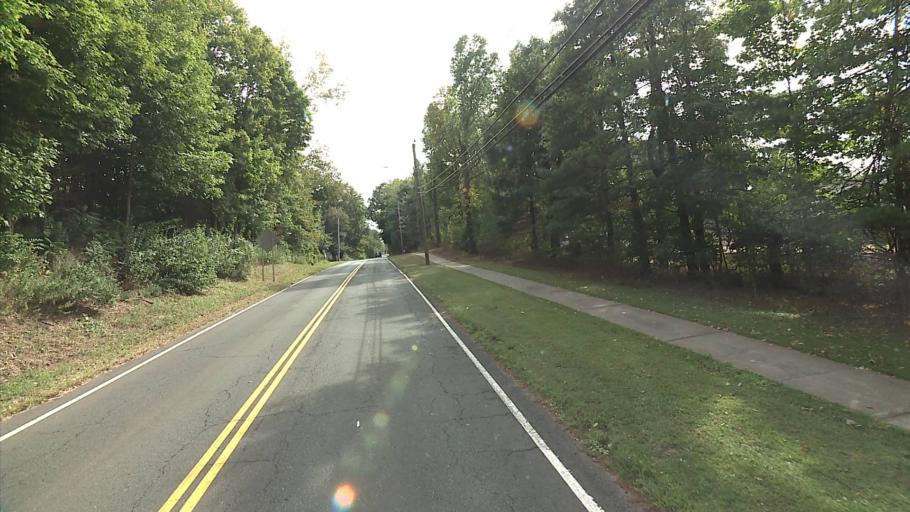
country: US
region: Connecticut
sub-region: Hartford County
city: Newington
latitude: 41.6750
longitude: -72.7195
